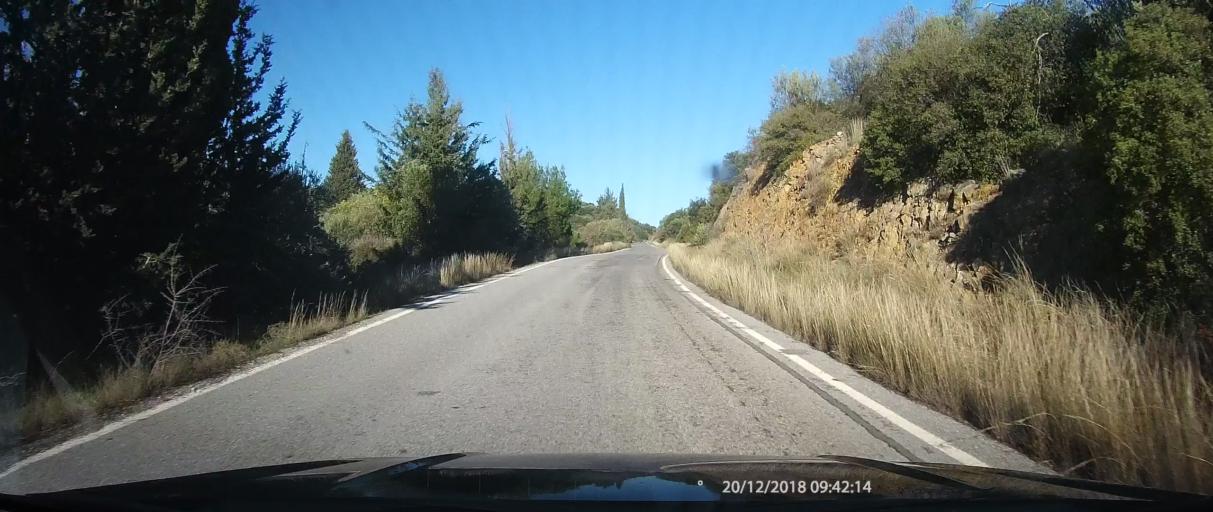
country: GR
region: Peloponnese
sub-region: Nomos Lakonias
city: Yerakion
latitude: 36.9574
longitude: 22.7571
